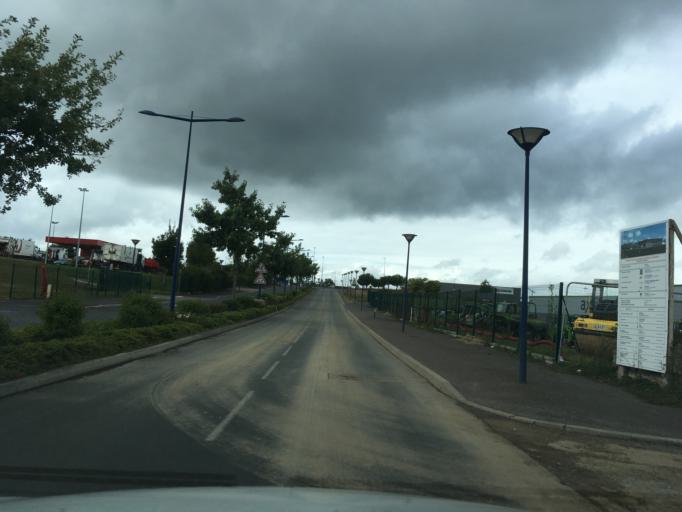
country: FR
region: Limousin
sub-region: Departement de la Correze
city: Saint-Pantaleon-de-Larche
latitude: 45.1395
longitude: 1.4732
